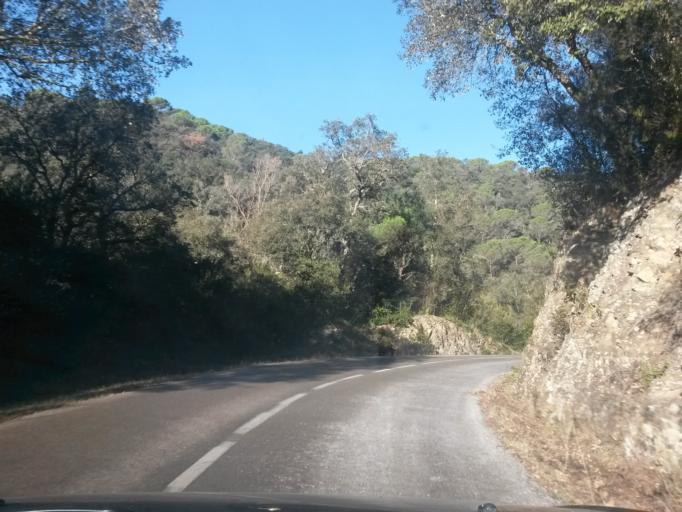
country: ES
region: Catalonia
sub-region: Provincia de Girona
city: Sant Gregori
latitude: 41.9884
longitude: 2.6812
